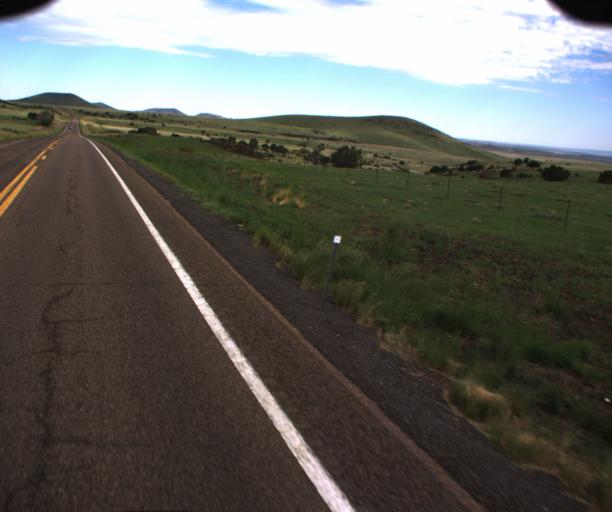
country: US
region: Arizona
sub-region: Apache County
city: Springerville
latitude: 34.2263
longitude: -109.4888
